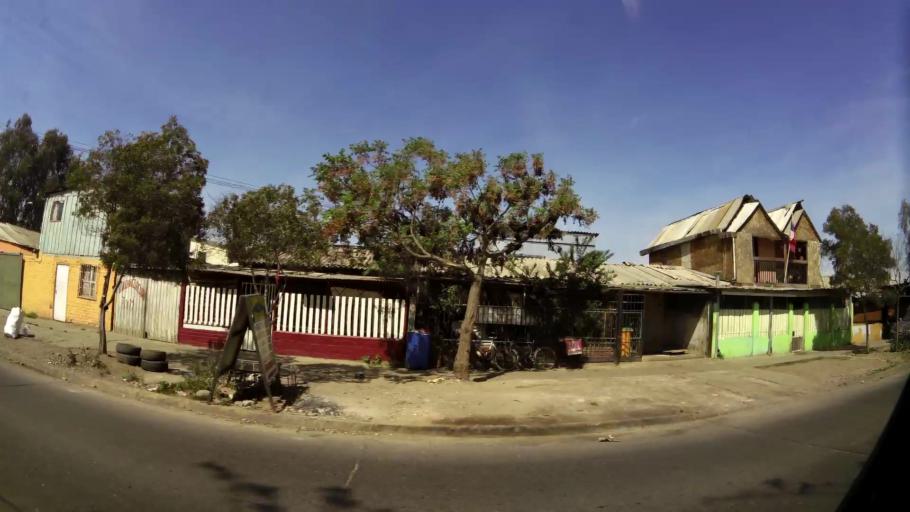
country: CL
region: Santiago Metropolitan
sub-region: Provincia de Maipo
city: San Bernardo
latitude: -33.5258
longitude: -70.6994
